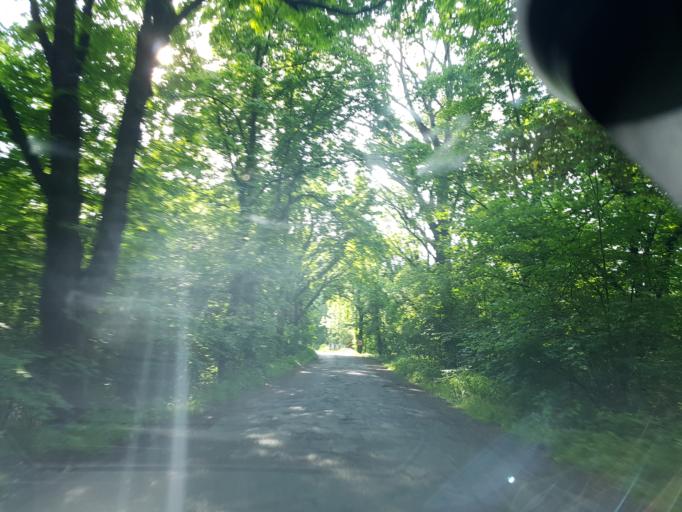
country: PL
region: Lower Silesian Voivodeship
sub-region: Powiat strzelinski
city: Wiazow
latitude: 50.8461
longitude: 17.2459
